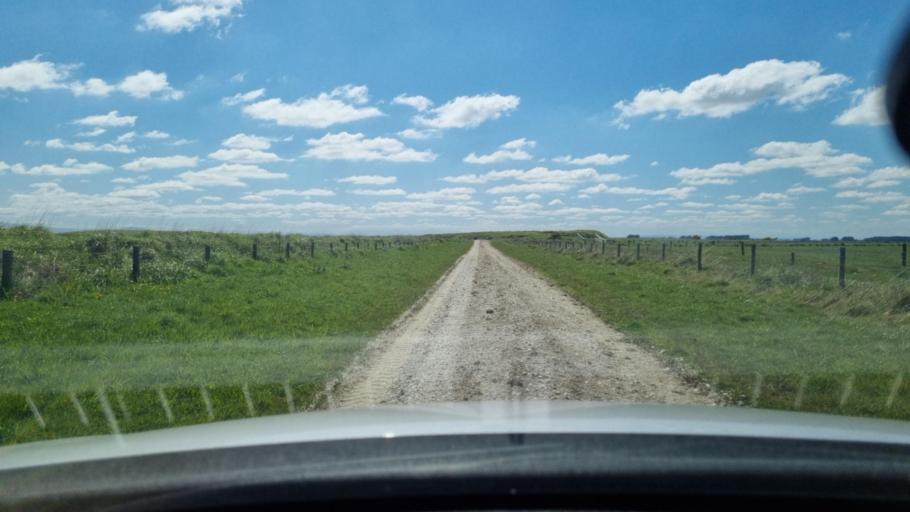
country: NZ
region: Southland
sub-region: Invercargill City
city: Invercargill
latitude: -46.3875
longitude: 168.2582
